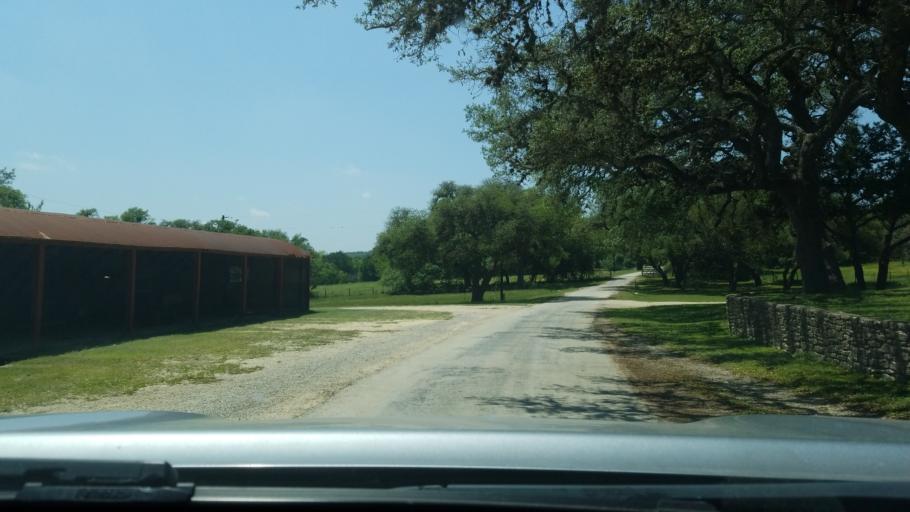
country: US
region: Texas
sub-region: Blanco County
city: Blanco
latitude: 30.0173
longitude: -98.4579
